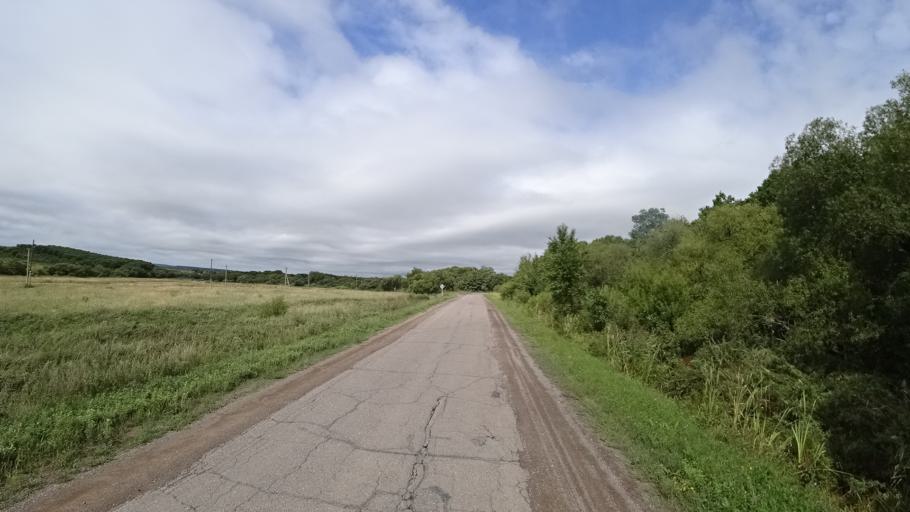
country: RU
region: Primorskiy
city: Lyalichi
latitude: 44.1513
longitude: 132.3912
